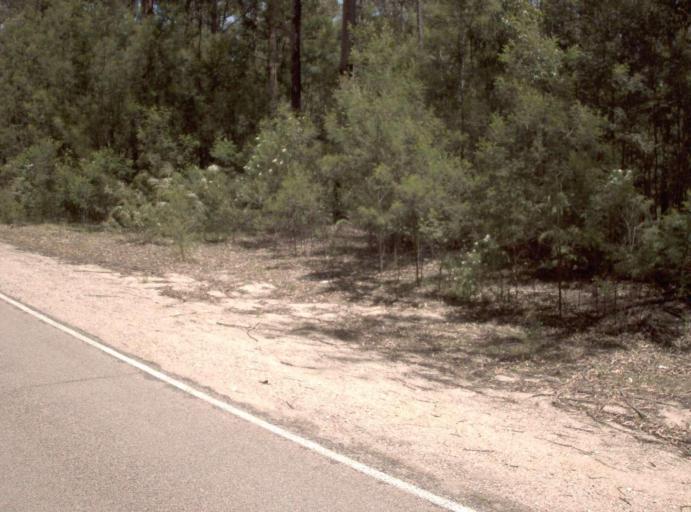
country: AU
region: Victoria
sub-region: East Gippsland
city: Lakes Entrance
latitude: -37.6377
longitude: 147.8966
